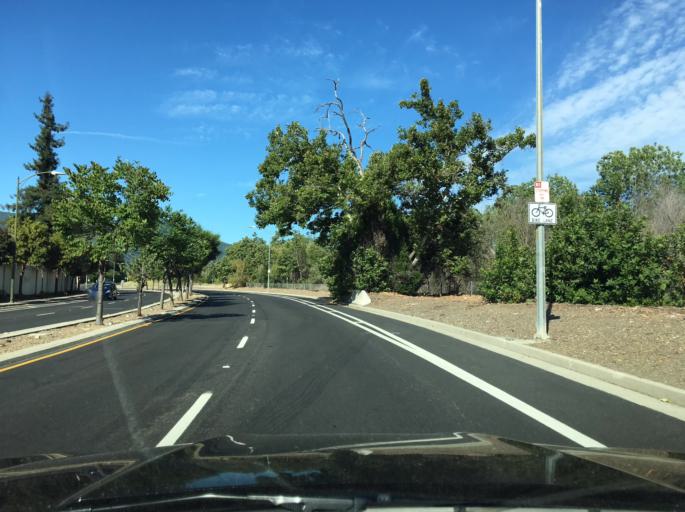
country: US
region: California
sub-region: Santa Clara County
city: Cambrian Park
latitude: 37.2399
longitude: -121.8833
